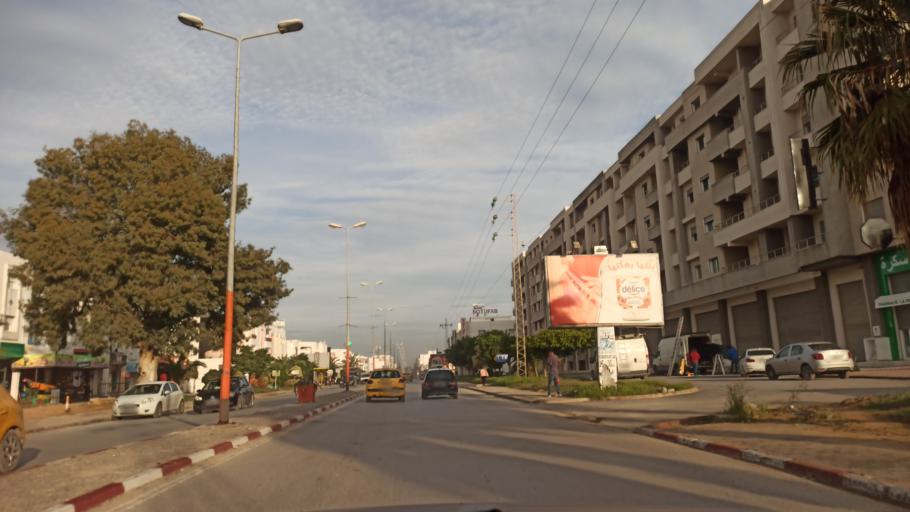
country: TN
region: Ariana
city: Ariana
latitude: 36.8621
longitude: 10.2543
